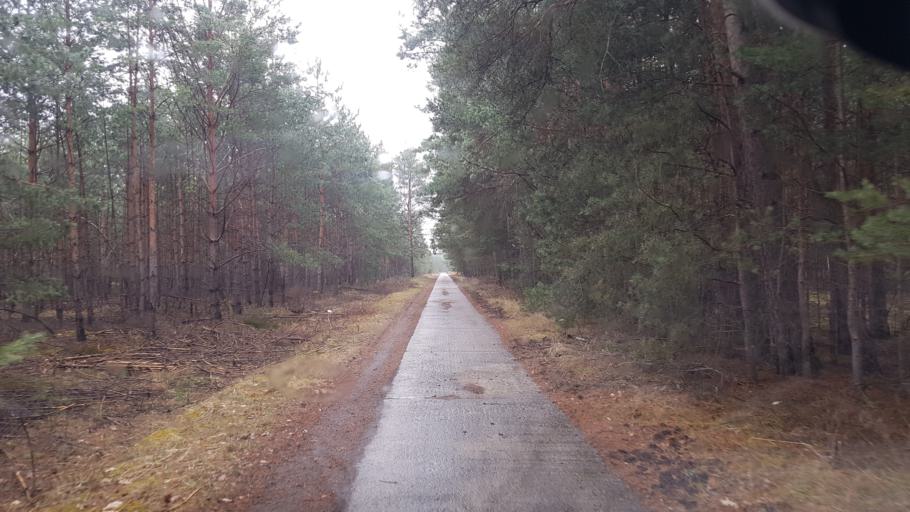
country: DE
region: Brandenburg
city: Grossraschen
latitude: 51.6047
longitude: 13.9895
